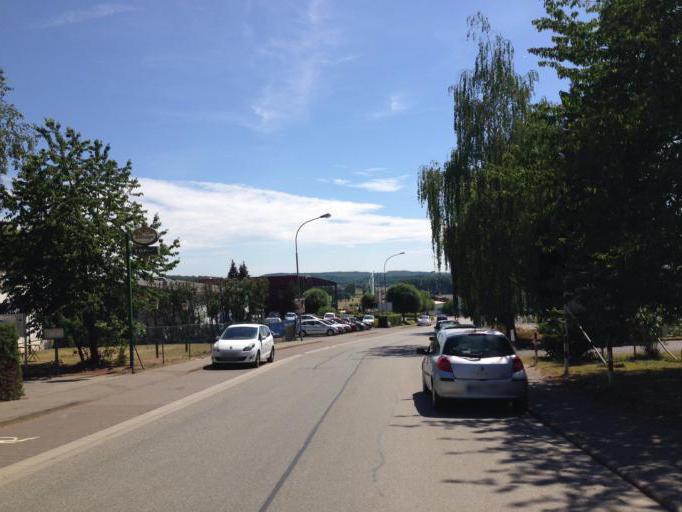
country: DE
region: Hesse
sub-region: Regierungsbezirk Giessen
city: Alten Buseck
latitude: 50.6183
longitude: 8.7351
